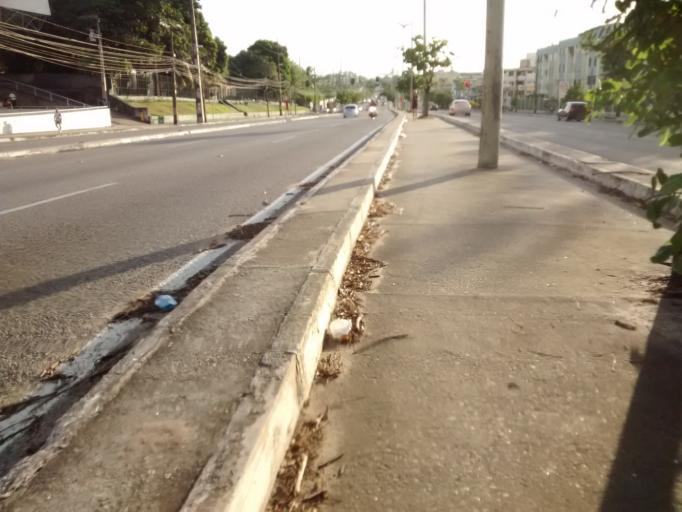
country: BR
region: Ceara
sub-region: Fortaleza
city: Fortaleza
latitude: -3.7368
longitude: -38.5706
